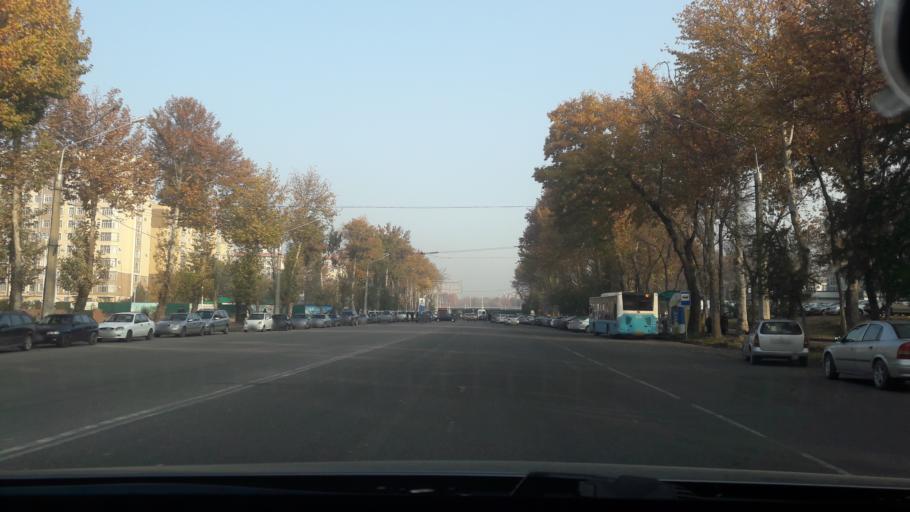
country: TJ
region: Dushanbe
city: Dushanbe
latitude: 38.5792
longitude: 68.7550
